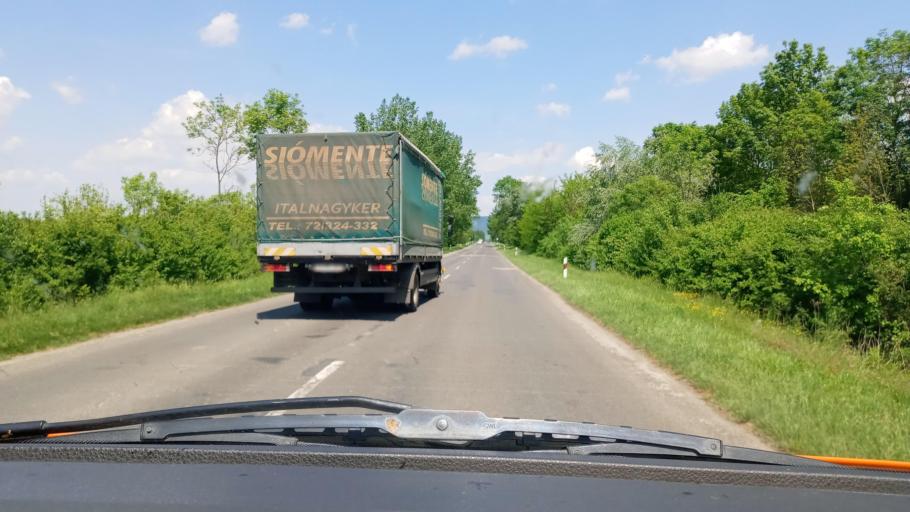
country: HU
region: Baranya
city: Harkany
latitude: 45.8234
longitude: 18.2189
